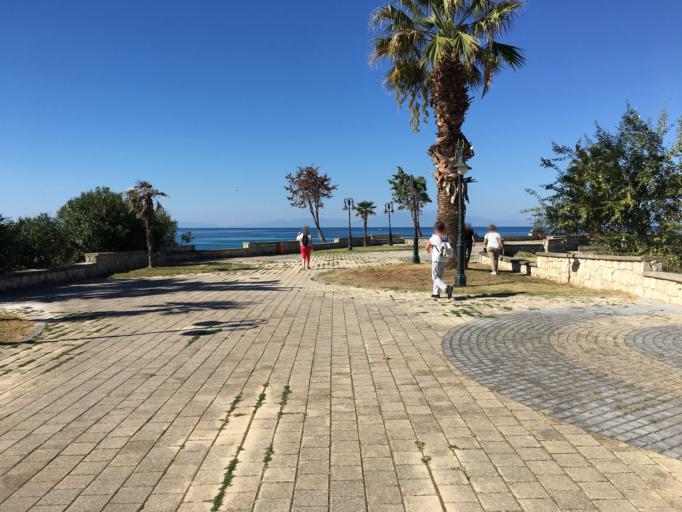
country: GR
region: Central Macedonia
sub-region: Nomos Chalkidikis
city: Nea Poteidaia
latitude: 40.1956
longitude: 23.3232
